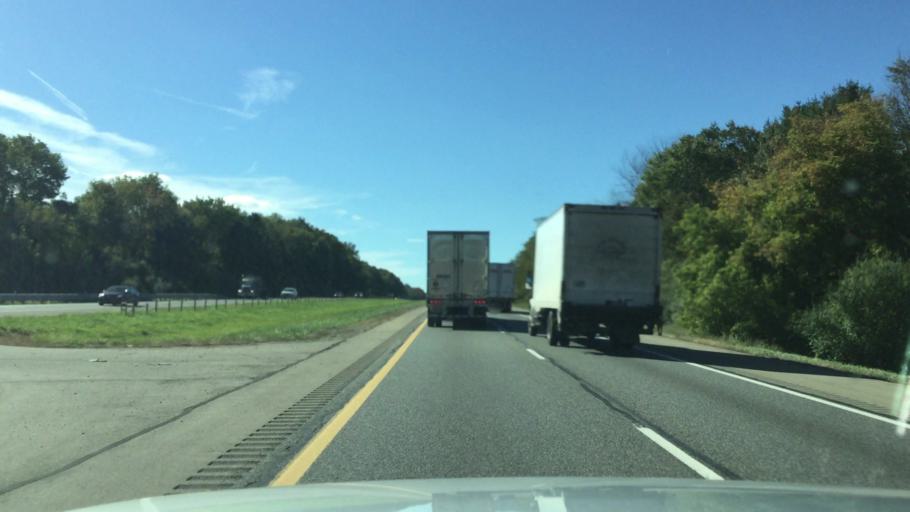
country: US
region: Michigan
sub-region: Washtenaw County
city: Dexter
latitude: 42.2976
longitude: -83.9044
